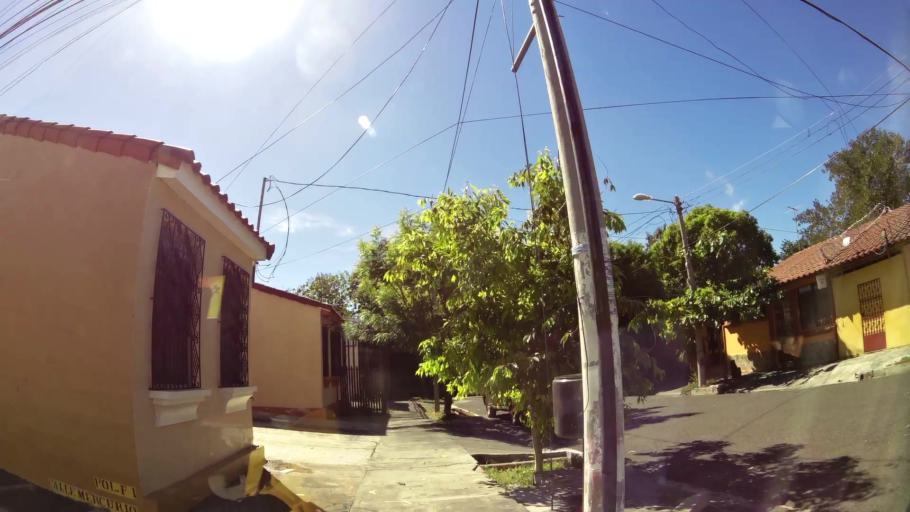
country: SV
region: San Miguel
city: San Miguel
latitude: 13.4916
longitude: -88.1671
